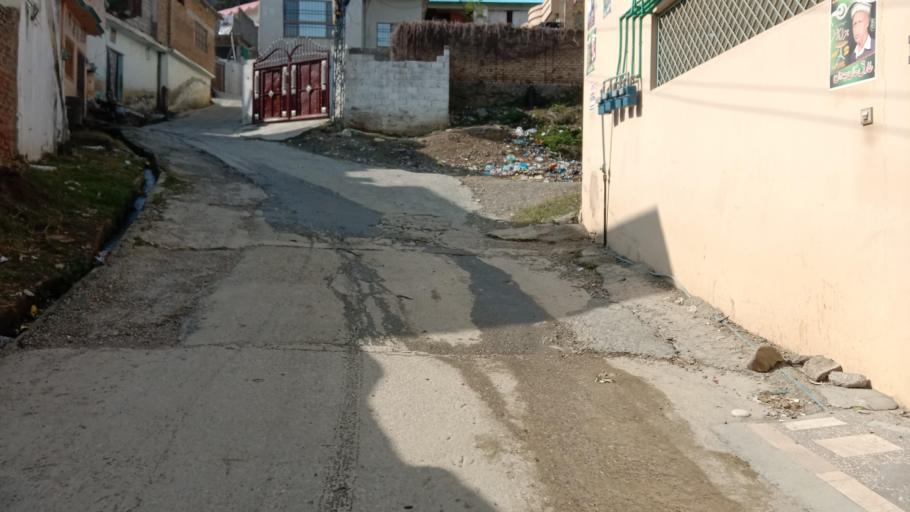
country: PK
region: Khyber Pakhtunkhwa
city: Abbottabad
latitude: 34.1770
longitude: 73.2117
